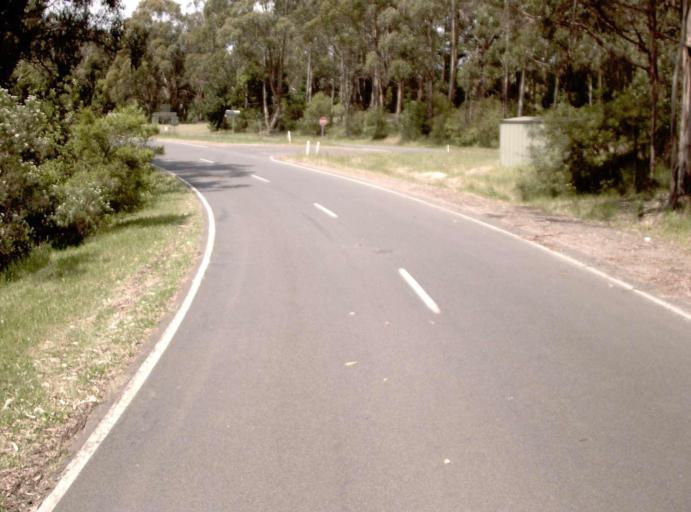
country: AU
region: Victoria
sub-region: Latrobe
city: Traralgon
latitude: -38.3503
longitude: 146.7139
